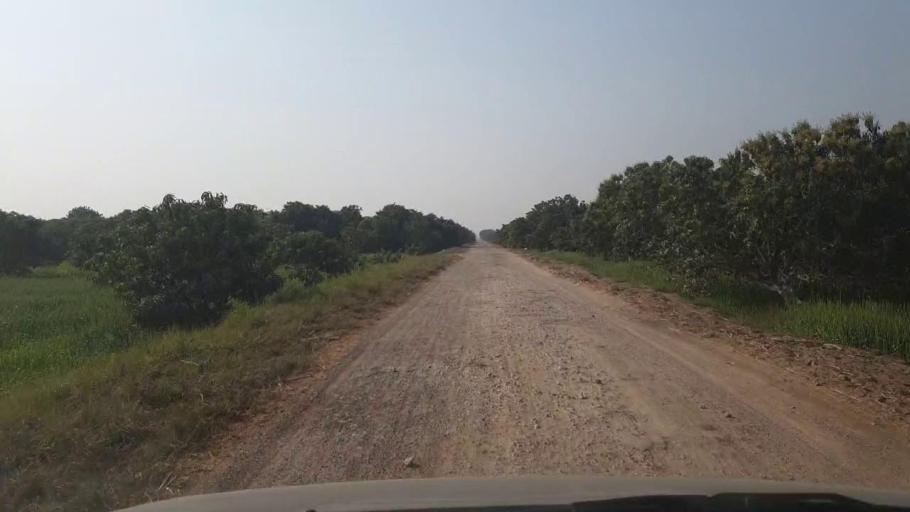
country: PK
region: Sindh
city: Mirwah Gorchani
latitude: 25.2619
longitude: 69.1512
